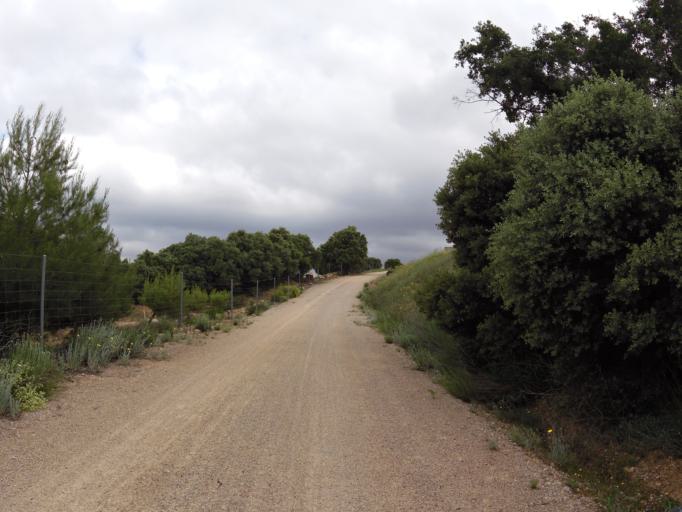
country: ES
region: Castille-La Mancha
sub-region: Provincia de Albacete
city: Robledo
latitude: 38.7338
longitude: -2.4669
